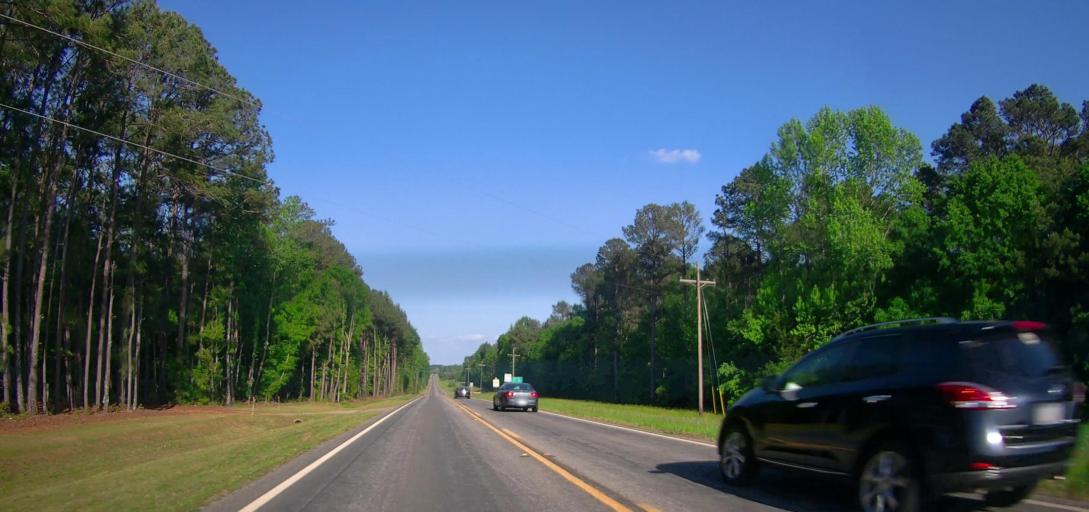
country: US
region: Georgia
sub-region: Walton County
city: Social Circle
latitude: 33.6240
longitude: -83.6311
